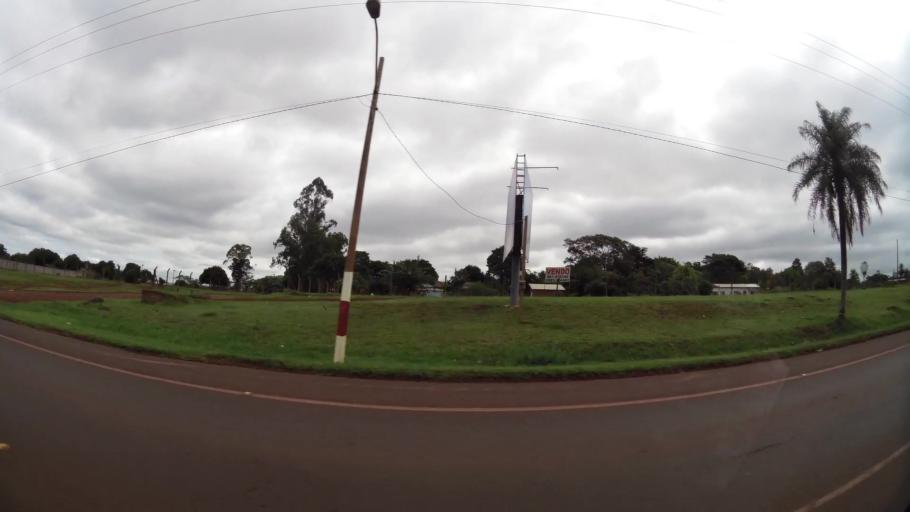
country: PY
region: Alto Parana
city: Ciudad del Este
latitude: -25.3967
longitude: -54.6350
